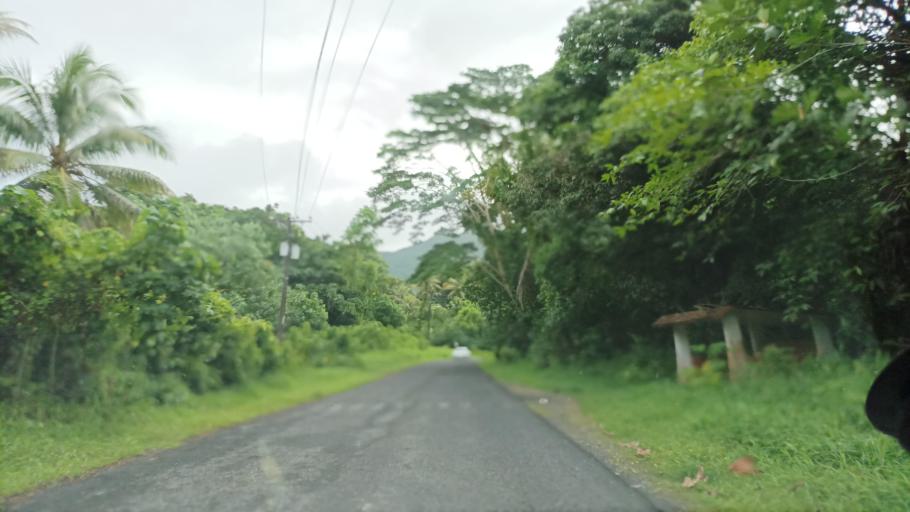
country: FM
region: Pohnpei
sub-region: Madolenihm Municipality
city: Madolenihm Municipality Government
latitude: 6.9145
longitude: 158.2925
